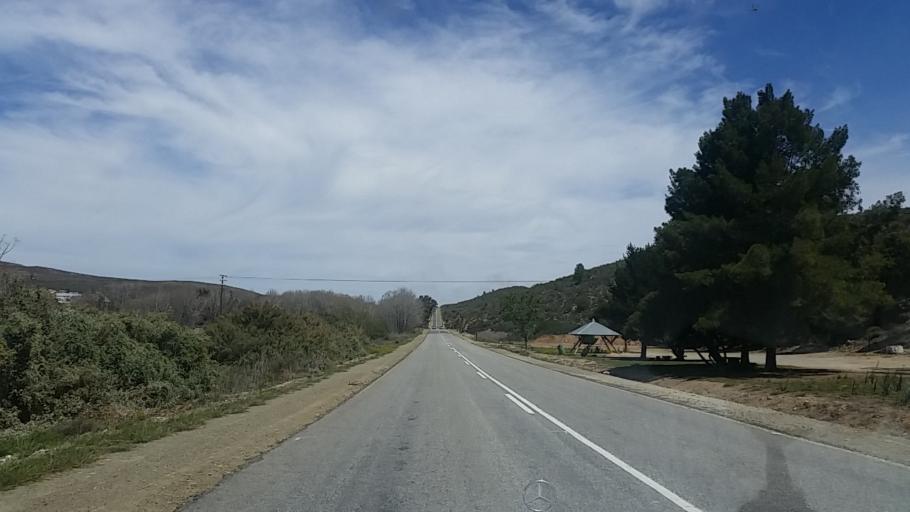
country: ZA
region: Western Cape
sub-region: Eden District Municipality
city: Knysna
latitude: -33.6507
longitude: 23.1264
